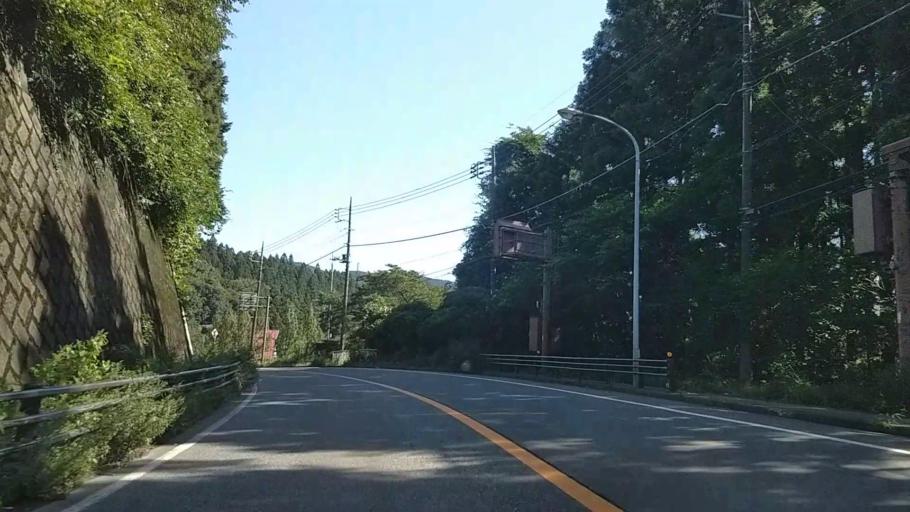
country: JP
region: Gunma
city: Annaka
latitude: 36.3339
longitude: 138.7171
